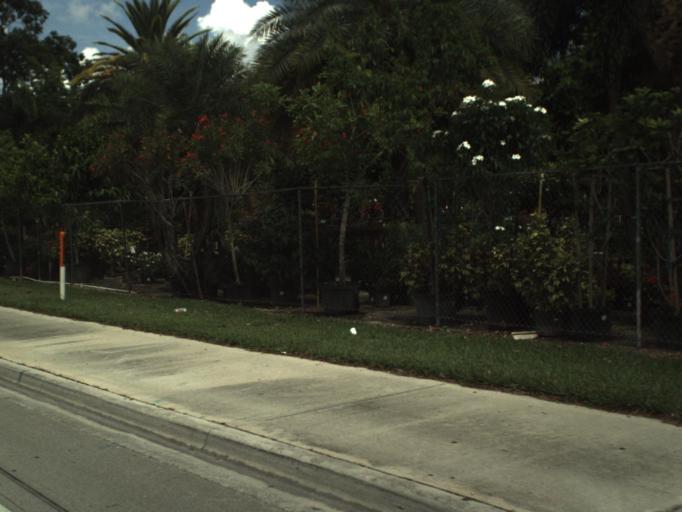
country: US
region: Florida
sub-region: Broward County
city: Davie
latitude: 26.0628
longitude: -80.1950
